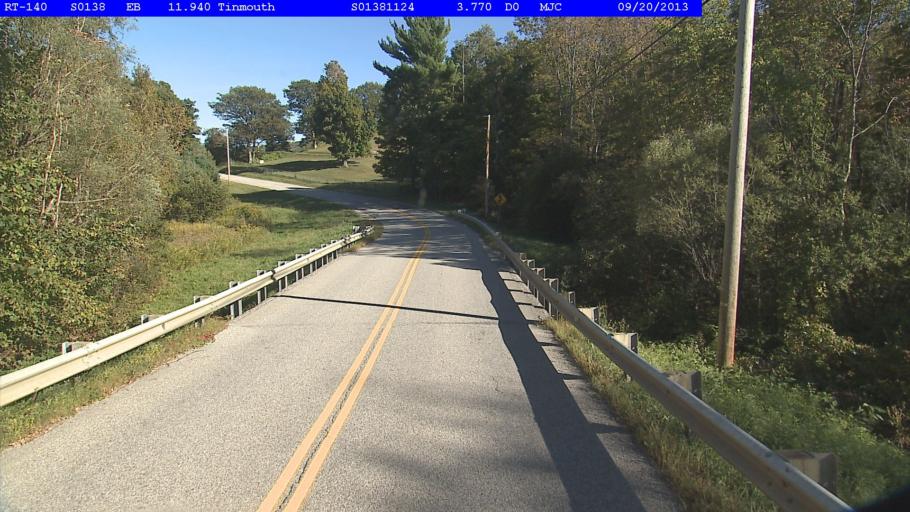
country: US
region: Vermont
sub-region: Rutland County
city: West Rutland
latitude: 43.4497
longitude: -73.0420
